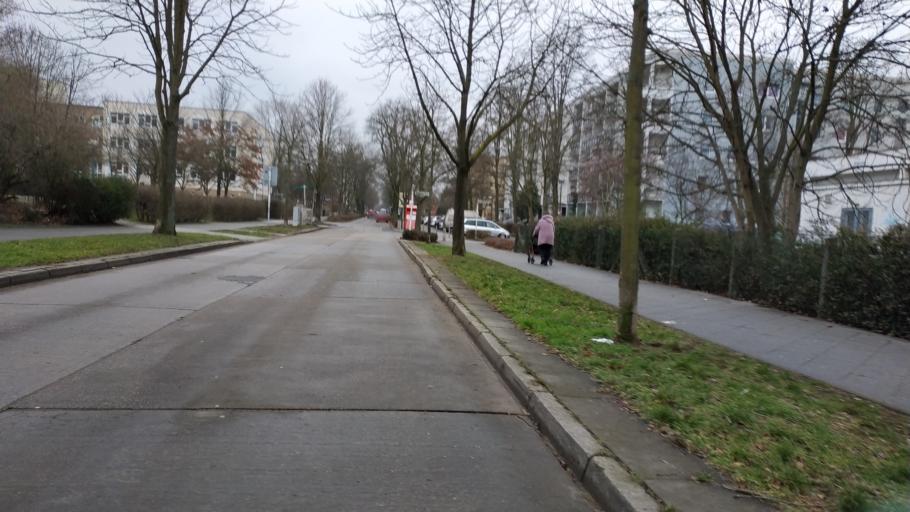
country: DE
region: Berlin
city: Hellersdorf
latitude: 52.5434
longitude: 13.5996
